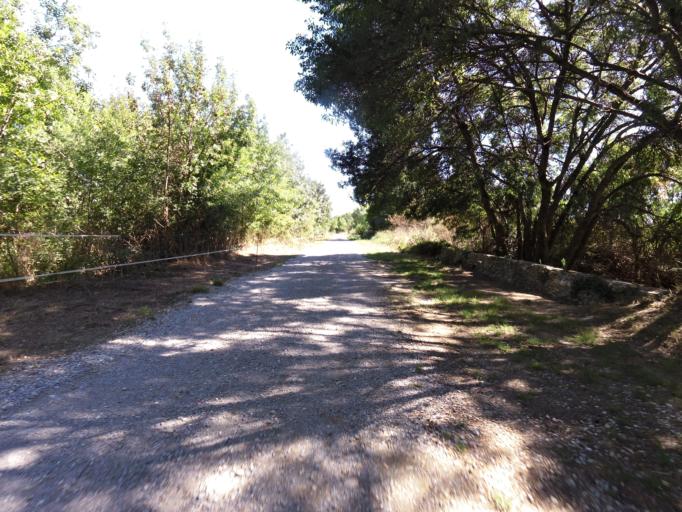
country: FR
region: Languedoc-Roussillon
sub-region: Departement du Gard
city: Vergeze
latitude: 43.7407
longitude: 4.2132
